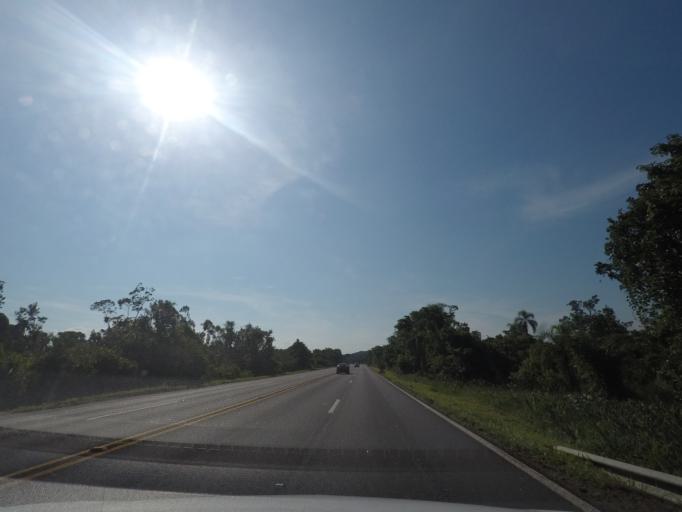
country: BR
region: Parana
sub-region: Paranagua
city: Paranagua
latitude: -25.5786
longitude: -48.6125
